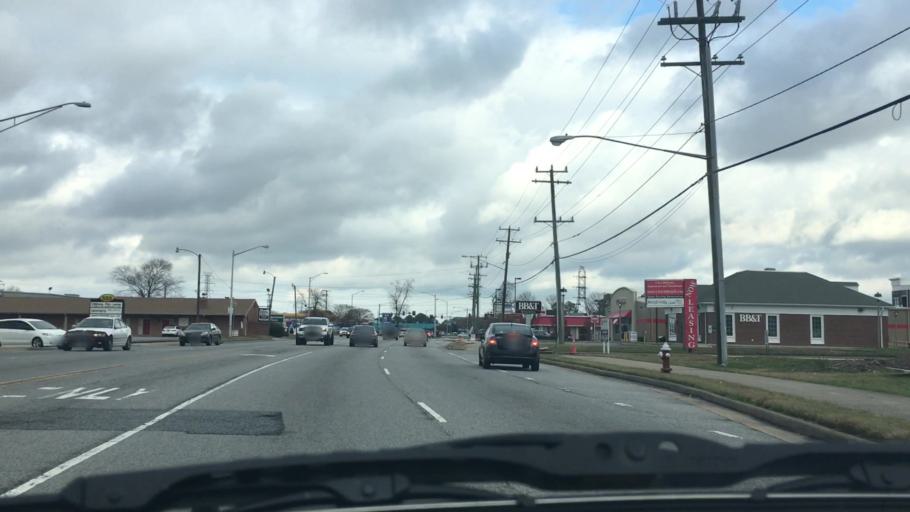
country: US
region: Virginia
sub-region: City of Chesapeake
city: Chesapeake
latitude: 36.8574
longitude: -76.1768
